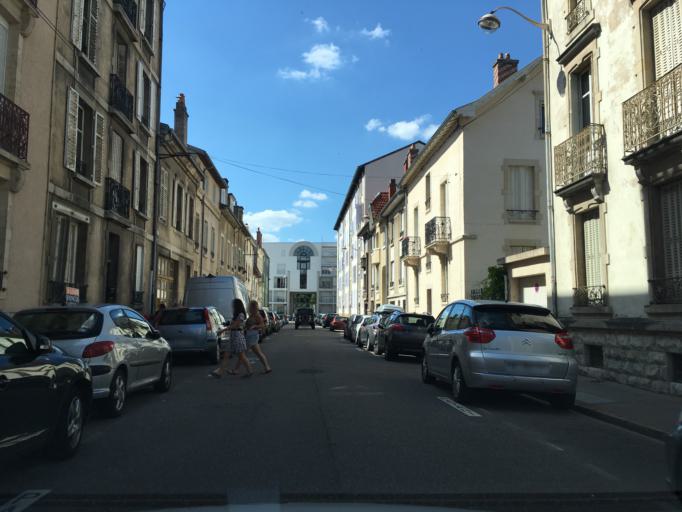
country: FR
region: Lorraine
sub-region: Departement de Meurthe-et-Moselle
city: Malzeville
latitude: 48.7027
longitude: 6.1803
